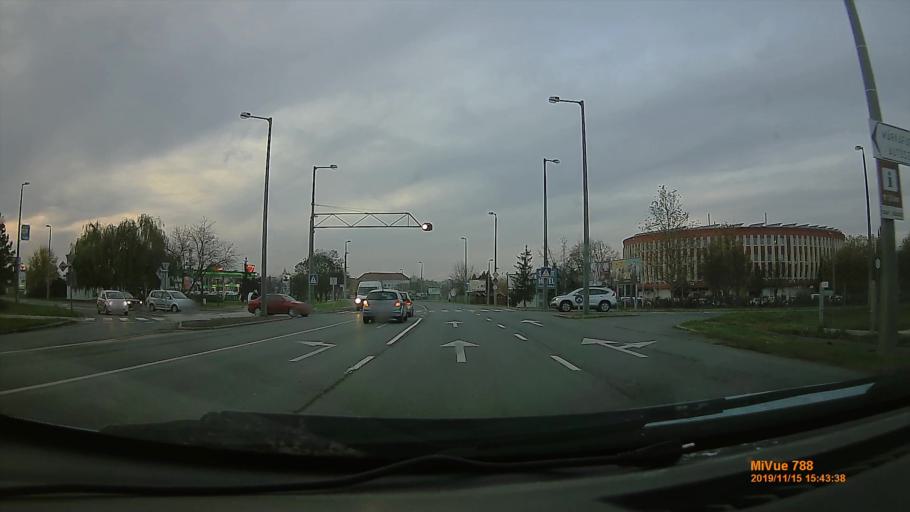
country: HU
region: Bekes
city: Bekescsaba
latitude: 46.6812
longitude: 21.1147
